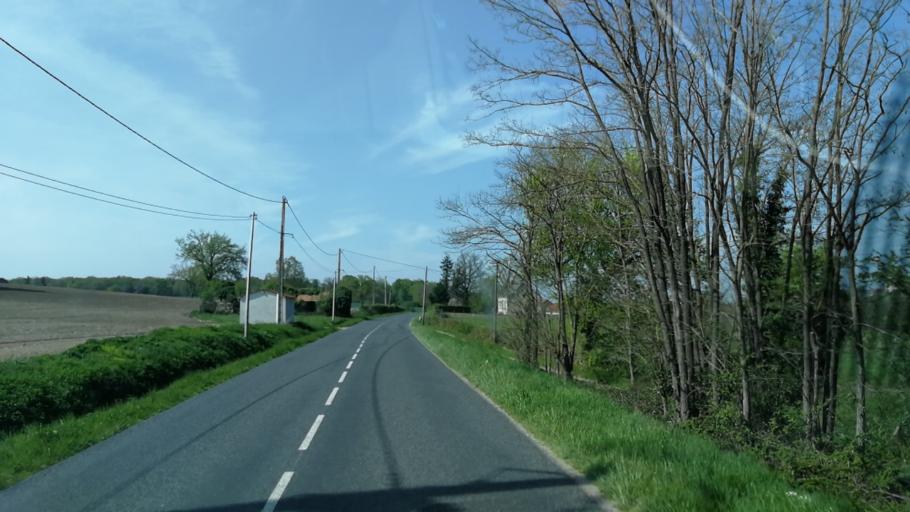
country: FR
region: Auvergne
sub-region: Departement de l'Allier
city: Saint-Gerand-le-Puy
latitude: 46.3393
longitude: 3.5802
